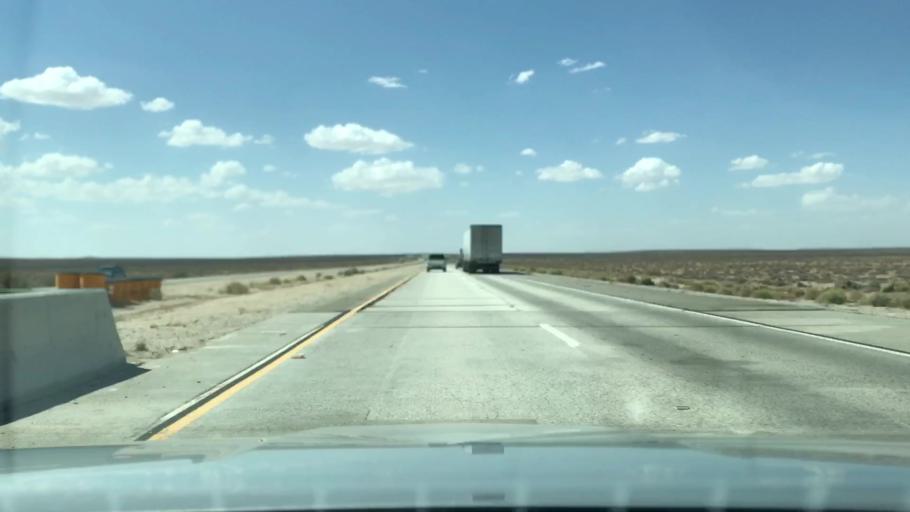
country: US
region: California
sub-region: San Bernardino County
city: Lenwood
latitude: 34.9345
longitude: -117.3713
